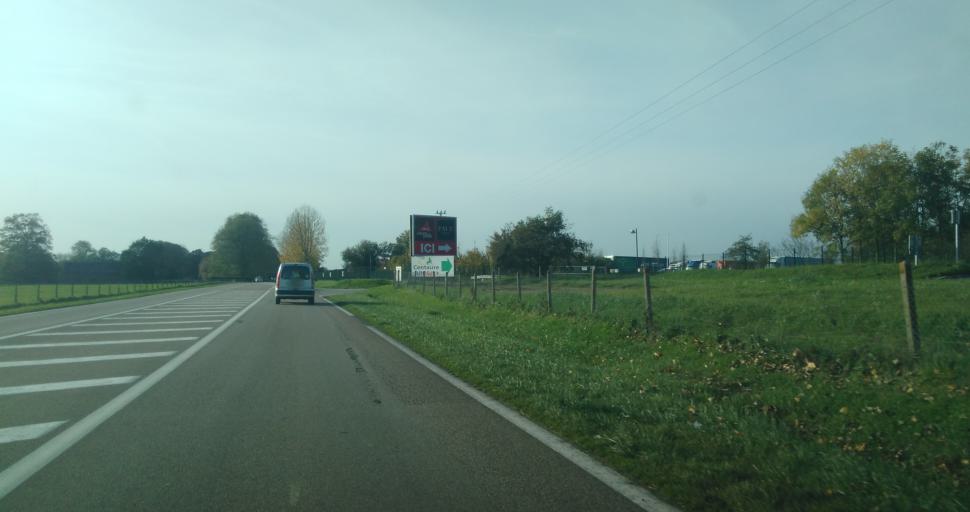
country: FR
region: Haute-Normandie
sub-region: Departement de l'Eure
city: Saint-Ouen-de-Thouberville
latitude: 49.3593
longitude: 0.8631
